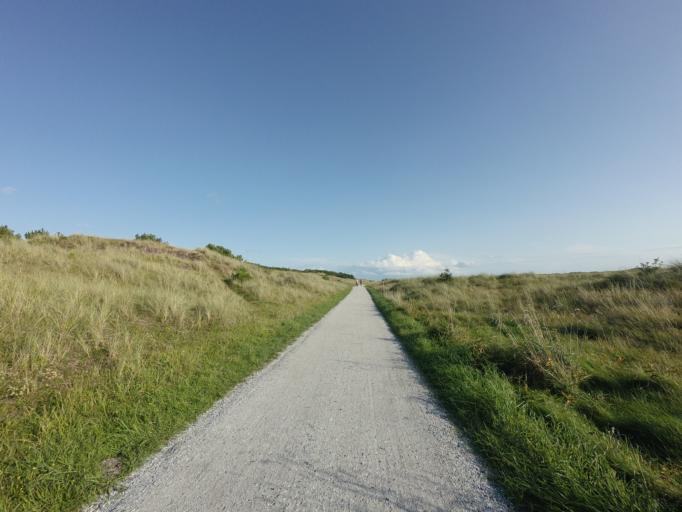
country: NL
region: Friesland
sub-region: Gemeente Terschelling
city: West-Terschelling
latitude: 53.3608
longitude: 5.2061
